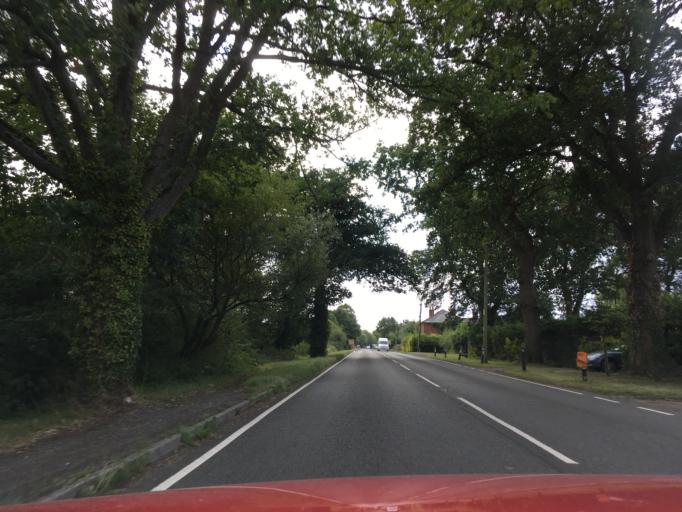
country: GB
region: England
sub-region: Hampshire
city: Bishops Waltham
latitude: 50.9751
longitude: -1.2609
